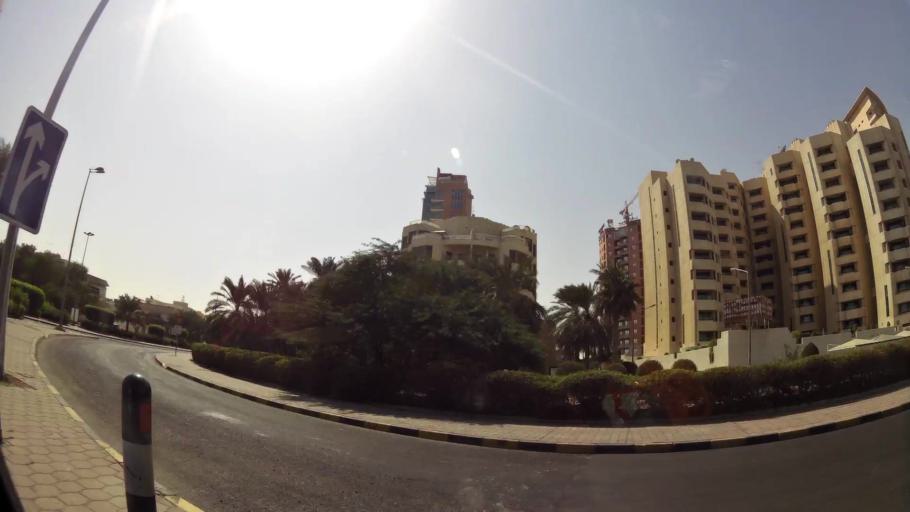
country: KW
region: Al Asimah
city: Ad Dasmah
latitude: 29.3689
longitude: 48.0124
